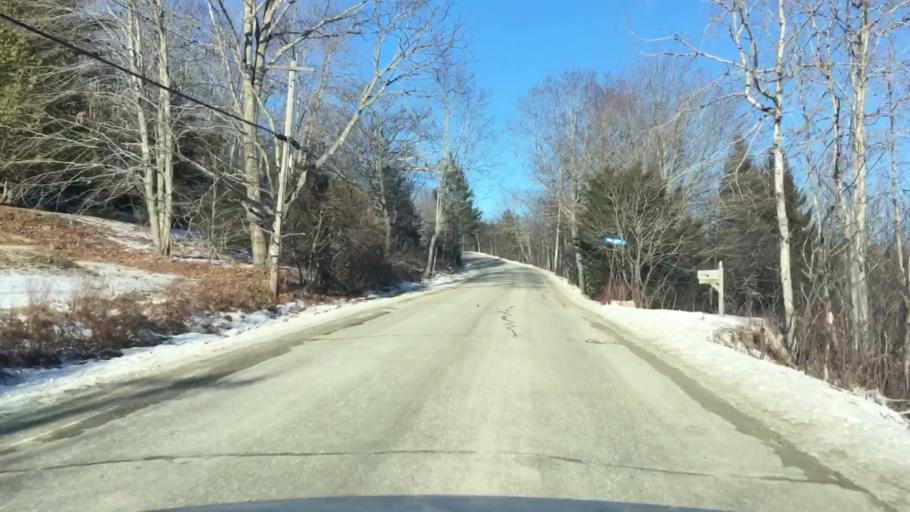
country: US
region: Maine
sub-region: Hancock County
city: Castine
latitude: 44.3509
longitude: -68.7809
